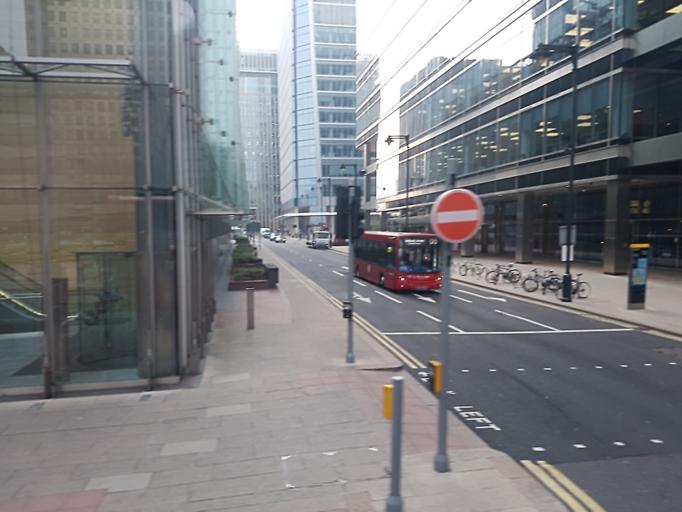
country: GB
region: England
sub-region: Greater London
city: Poplar
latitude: 51.5047
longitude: -0.0172
